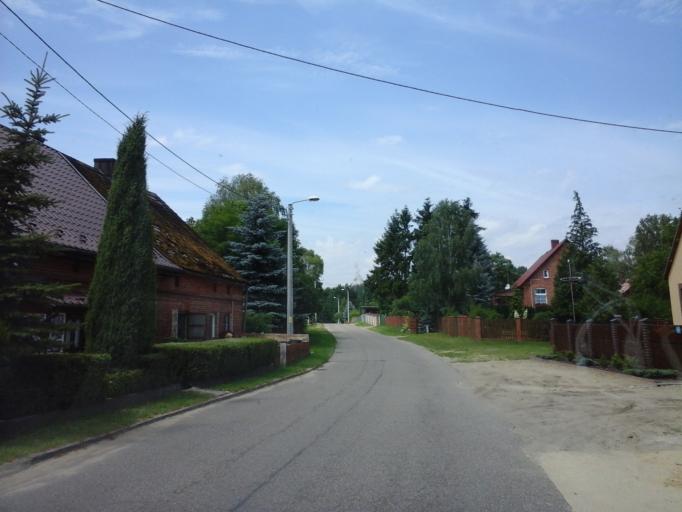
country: PL
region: West Pomeranian Voivodeship
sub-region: Powiat choszczenski
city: Bierzwnik
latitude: 53.0419
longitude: 15.6448
